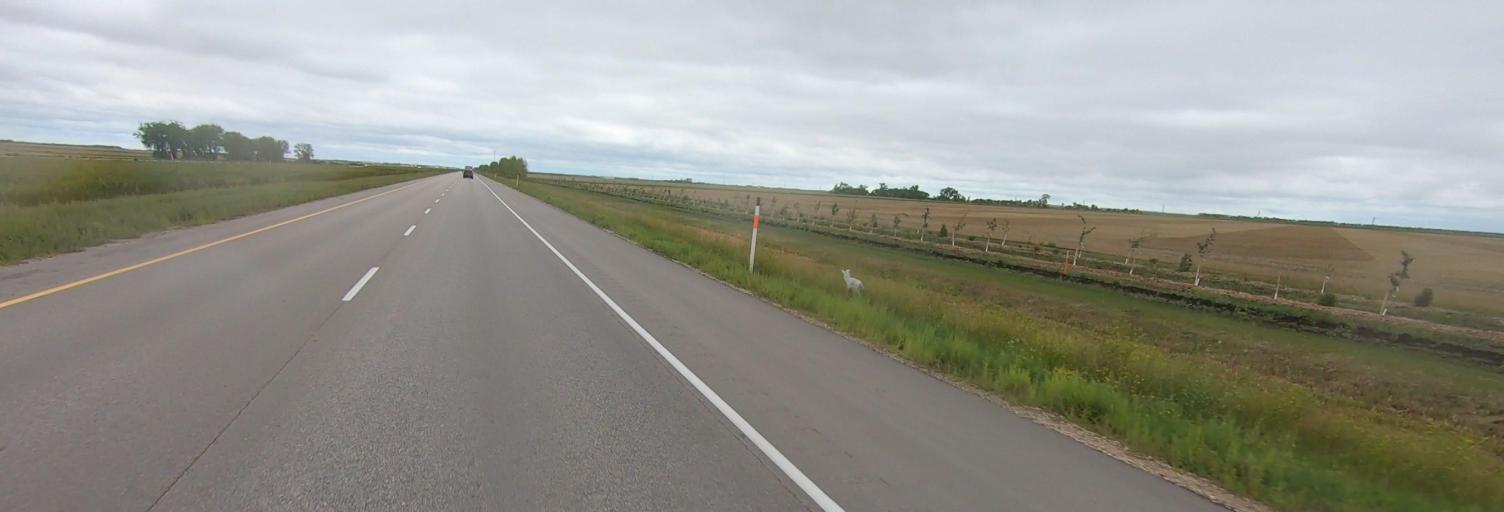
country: CA
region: Manitoba
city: Headingley
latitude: 49.8887
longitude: -97.6592
